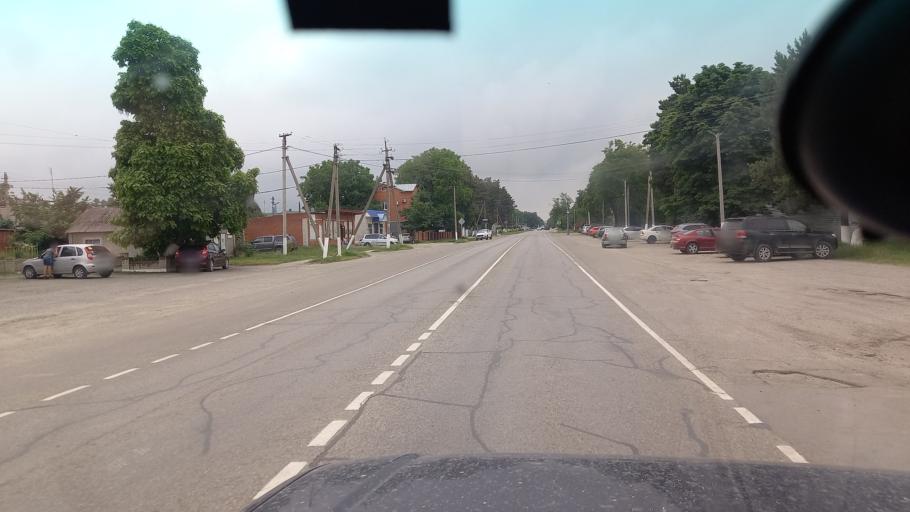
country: RU
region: Krasnodarskiy
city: Mostovskoy
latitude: 44.4122
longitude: 40.8034
